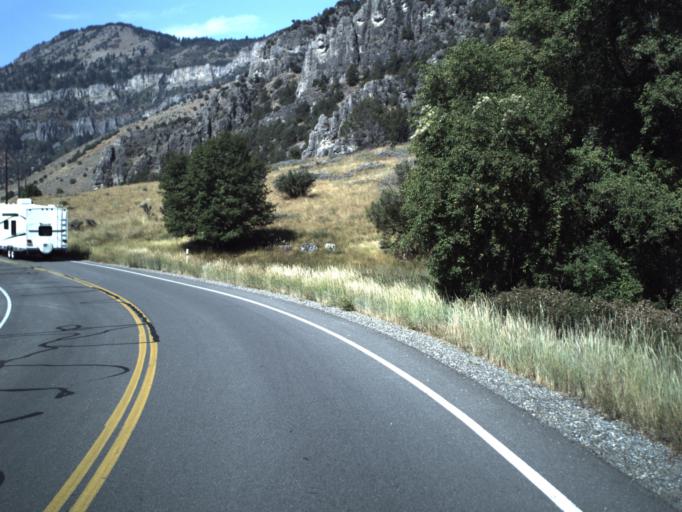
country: US
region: Utah
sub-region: Cache County
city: Millville
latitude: 41.6295
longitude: -111.6966
